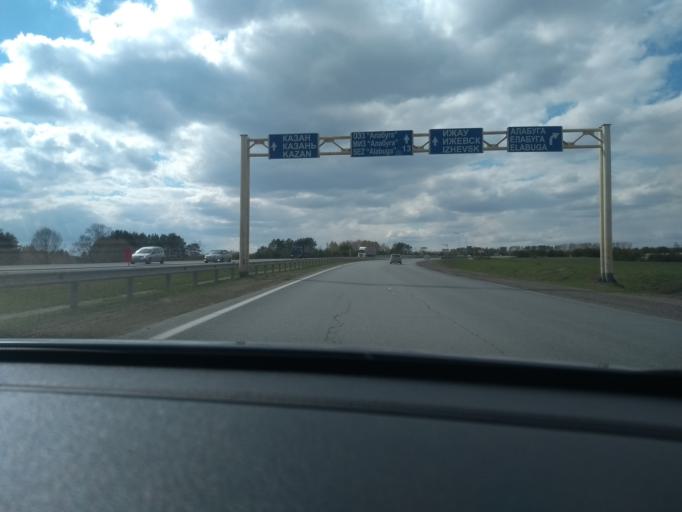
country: RU
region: Tatarstan
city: Yelabuga
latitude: 55.7815
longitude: 52.1809
